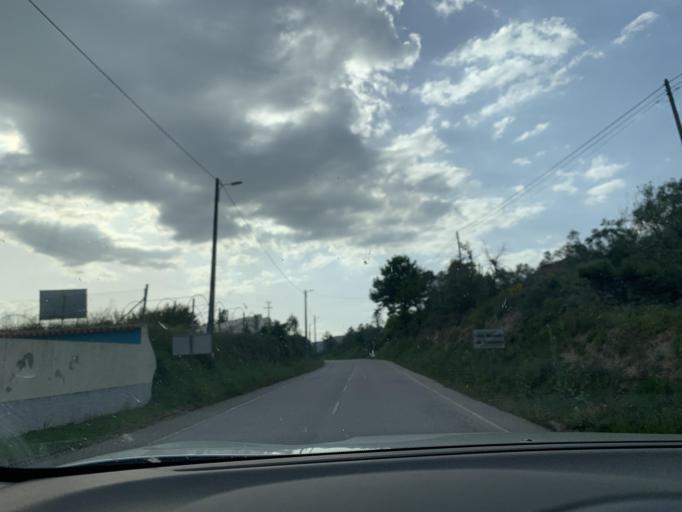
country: PT
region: Guarda
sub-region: Fornos de Algodres
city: Fornos de Algodres
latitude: 40.5796
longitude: -7.6125
